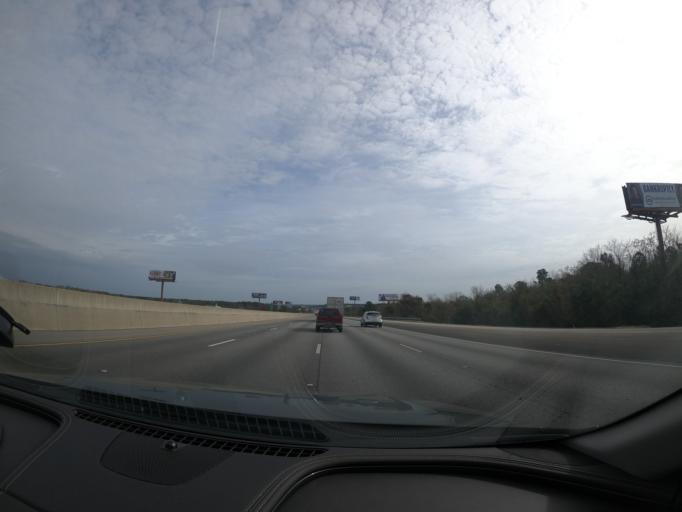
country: US
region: Georgia
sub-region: Columbia County
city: Martinez
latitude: 33.4892
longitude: -82.1039
